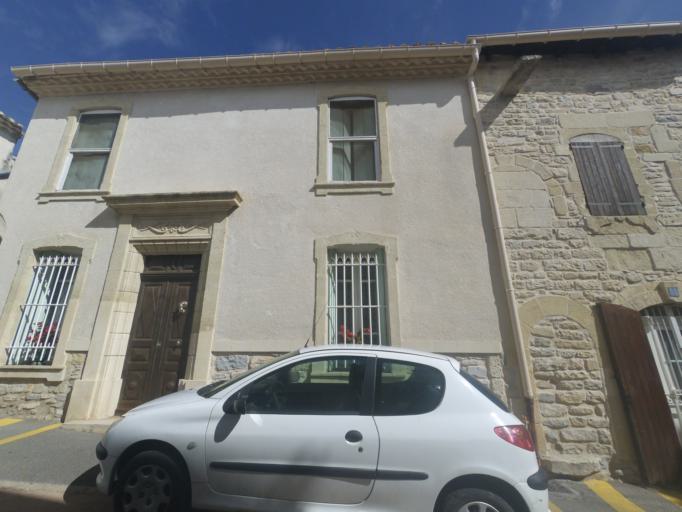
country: FR
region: Languedoc-Roussillon
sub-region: Departement du Gard
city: Nages-et-Solorgues
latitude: 43.7911
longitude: 4.2296
